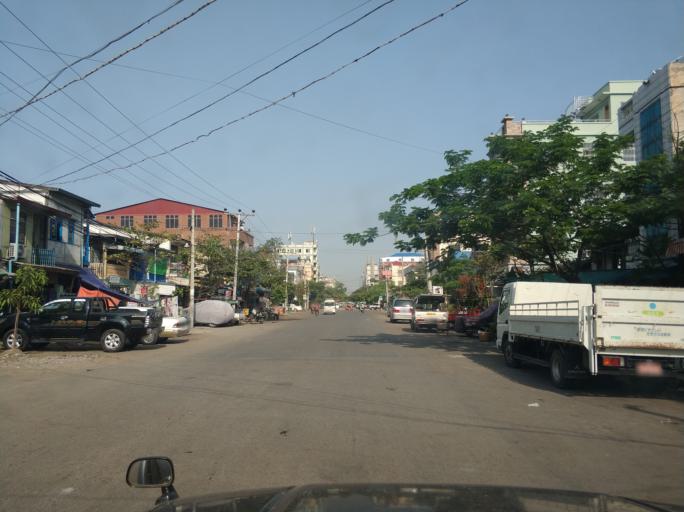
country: MM
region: Mandalay
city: Mandalay
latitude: 21.9704
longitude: 96.0925
